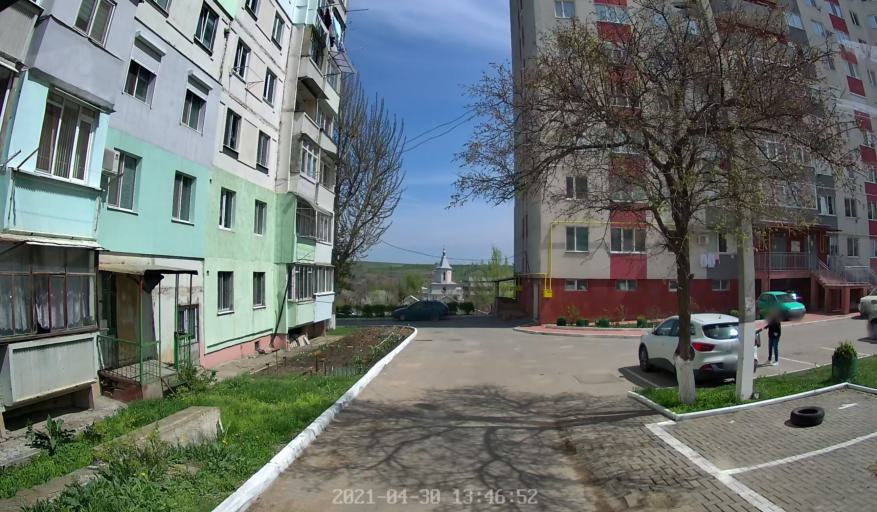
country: NG
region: Niger
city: Lemu
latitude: 9.4122
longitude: 5.7788
